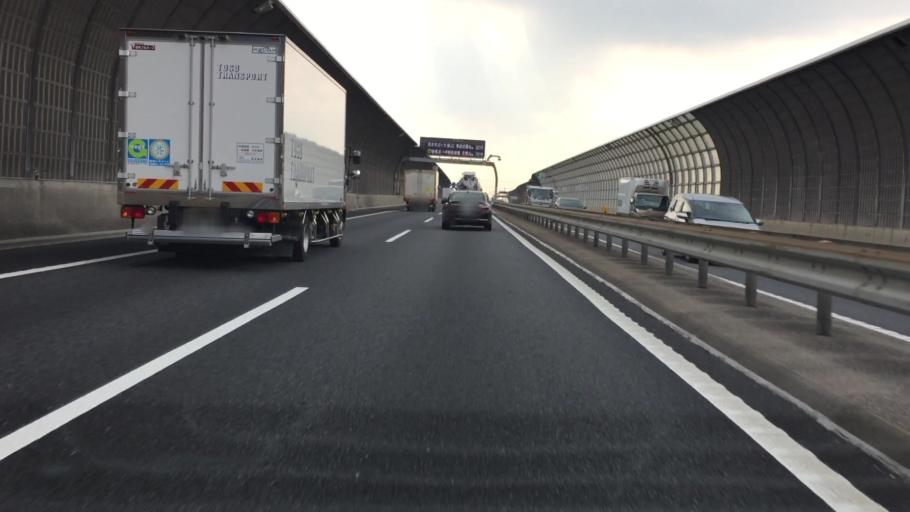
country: JP
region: Saitama
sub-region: Kawaguchi-shi
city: Hatogaya-honcho
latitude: 35.8515
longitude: 139.7533
